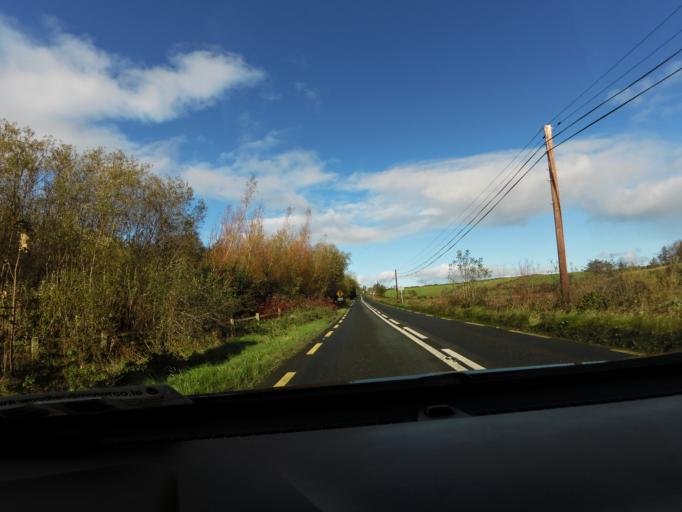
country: IE
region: Connaught
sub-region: Maigh Eo
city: Westport
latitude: 53.8179
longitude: -9.5324
